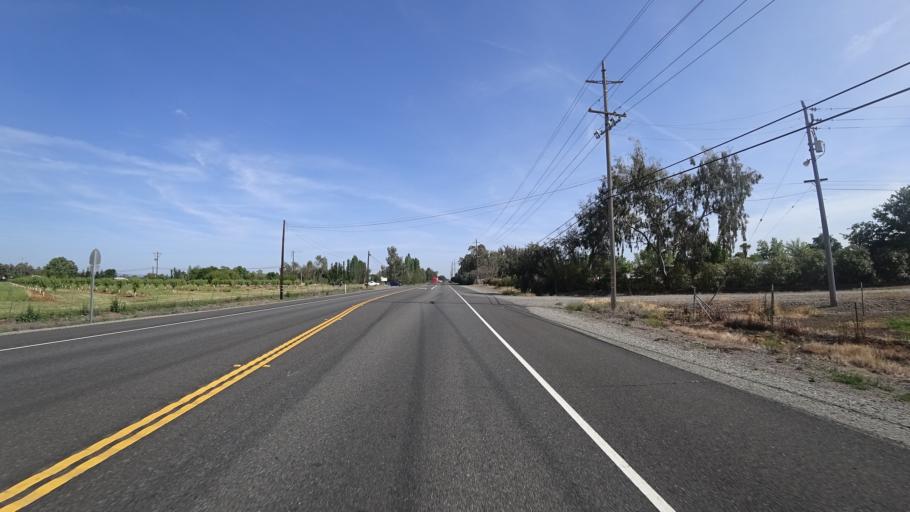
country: US
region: California
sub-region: Glenn County
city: Hamilton City
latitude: 39.8226
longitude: -121.9251
